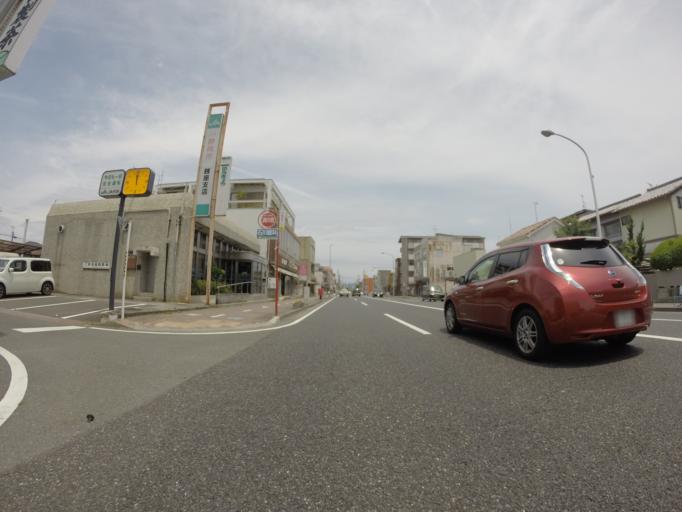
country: JP
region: Shizuoka
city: Shizuoka-shi
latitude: 34.9871
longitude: 138.3964
